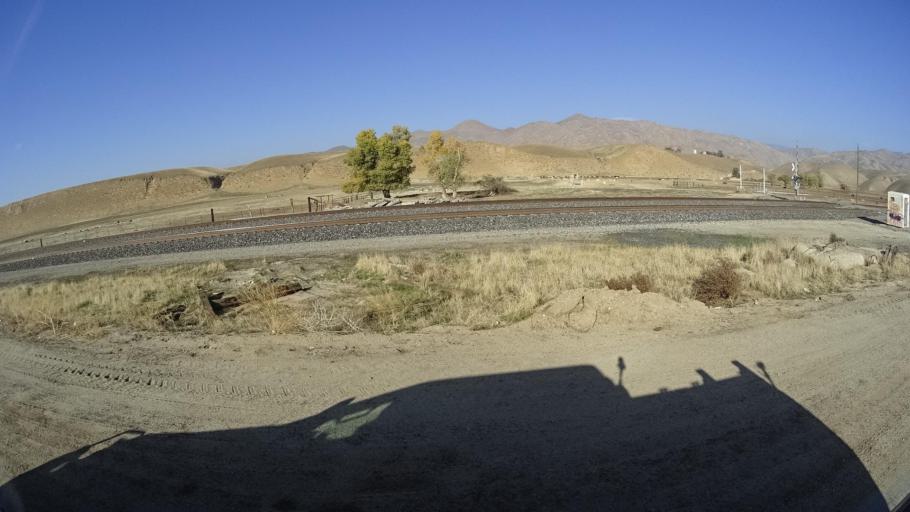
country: US
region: California
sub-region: Kern County
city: Arvin
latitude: 35.3268
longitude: -118.7418
